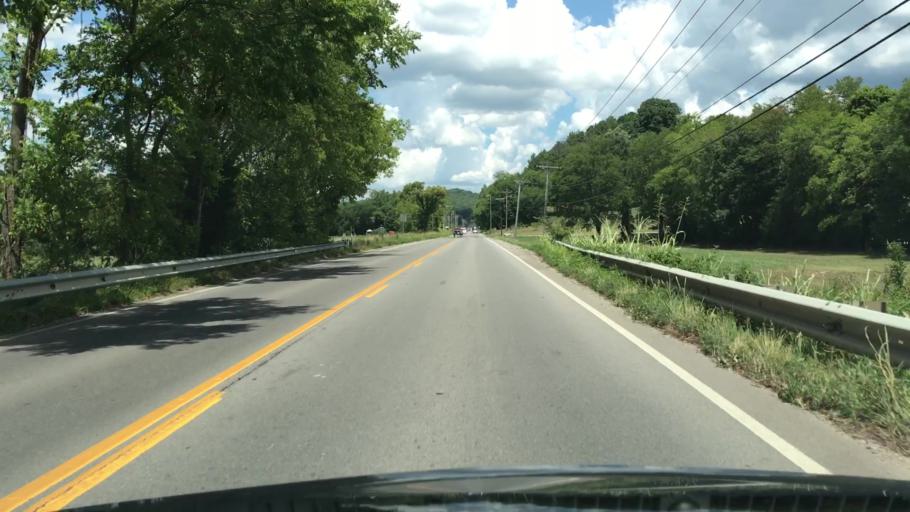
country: US
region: Tennessee
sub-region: Williamson County
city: Nolensville
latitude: 35.8843
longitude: -86.6629
